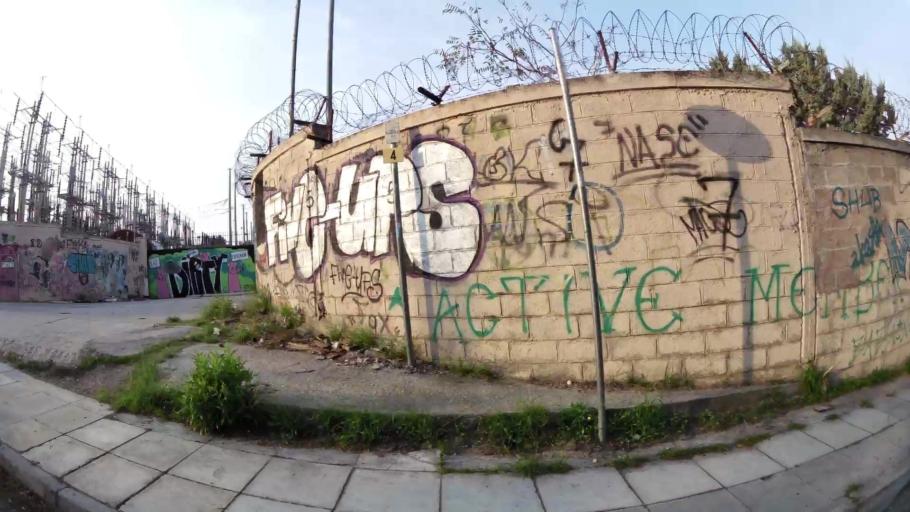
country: GR
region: Attica
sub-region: Nomarchia Athinas
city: Nea Smyrni
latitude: 37.9383
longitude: 23.7226
